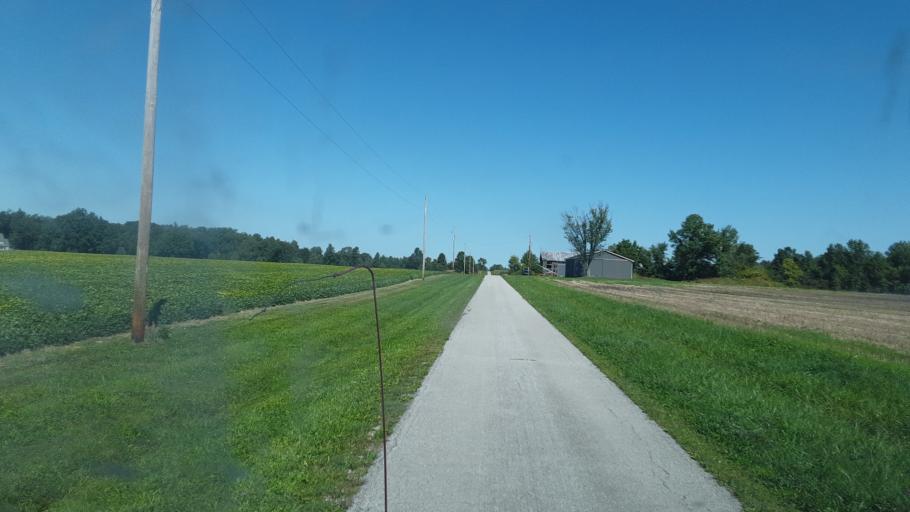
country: US
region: Ohio
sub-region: Sandusky County
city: Mount Carmel
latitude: 41.1490
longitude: -82.9189
